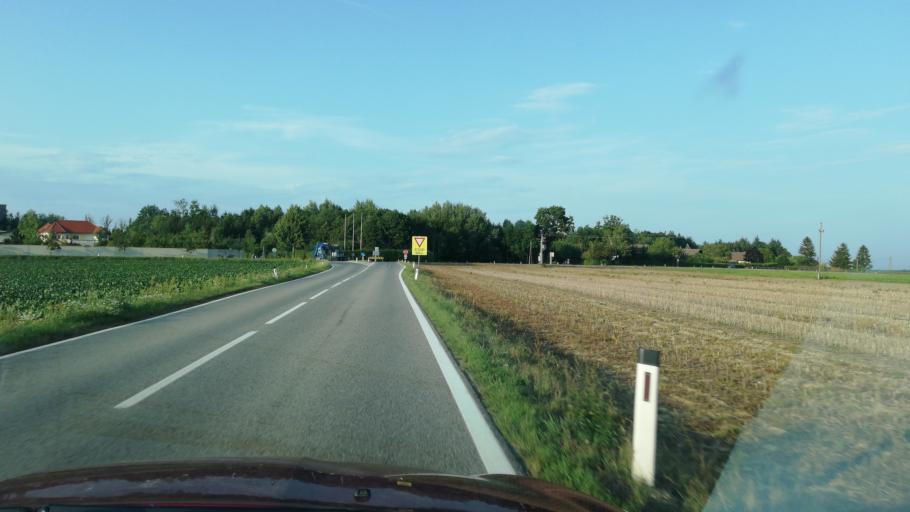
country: AT
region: Upper Austria
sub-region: Politischer Bezirk Steyr-Land
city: Sierning
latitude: 48.1227
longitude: 14.3390
